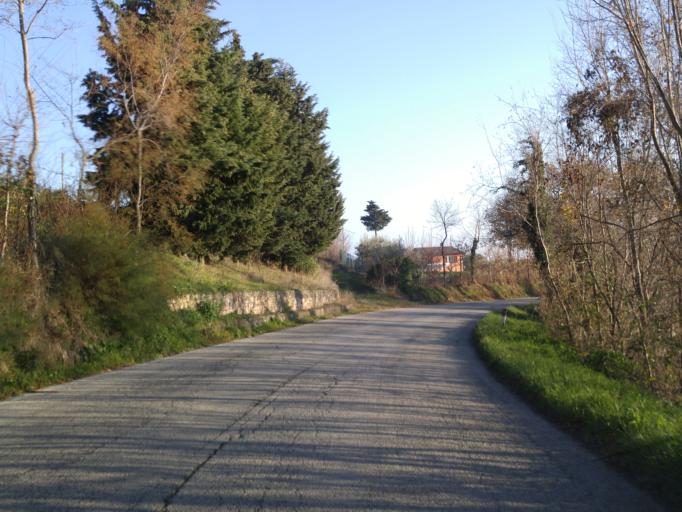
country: IT
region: The Marches
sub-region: Provincia di Pesaro e Urbino
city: Cartoceto
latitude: 43.7701
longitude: 12.8637
